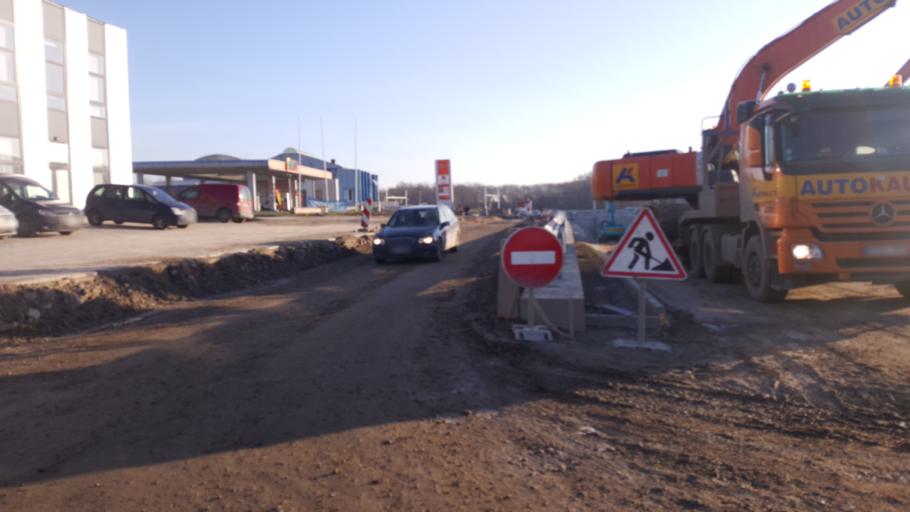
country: LT
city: Ramuciai
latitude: 54.9011
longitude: 24.0298
